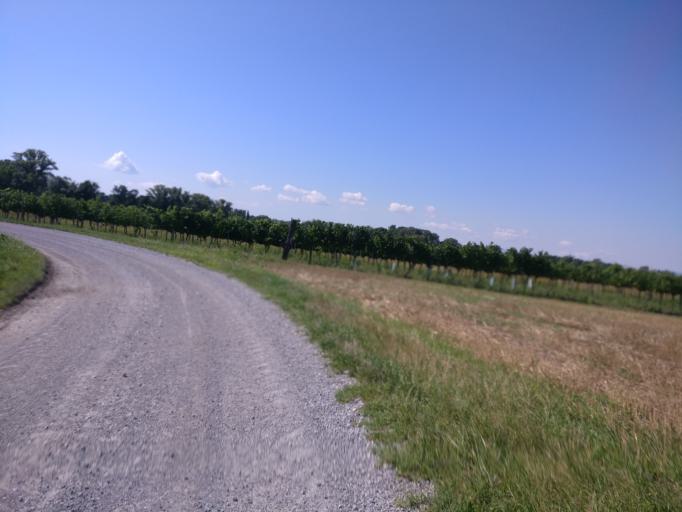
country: AT
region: Lower Austria
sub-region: Politischer Bezirk Baden
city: Pottendorf
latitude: 47.9114
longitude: 16.3531
